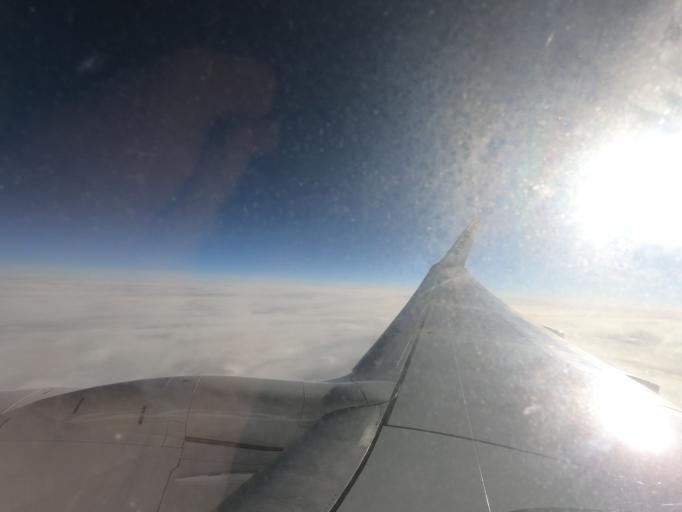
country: DE
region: Rheinland-Pfalz
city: Pelm
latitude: 50.2432
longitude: 6.6861
